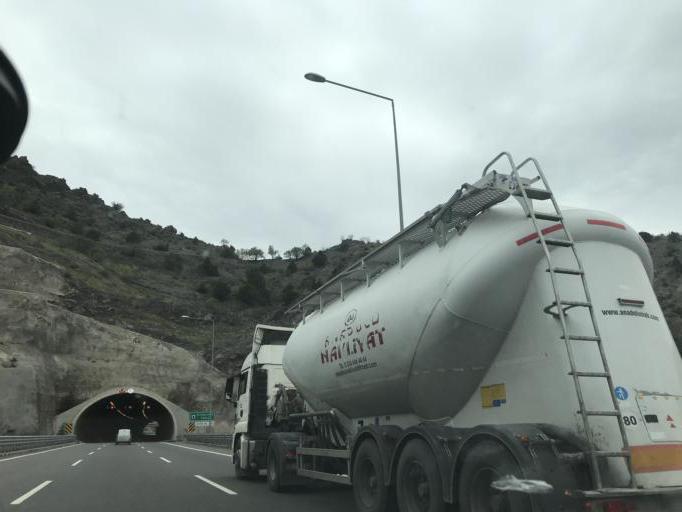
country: TR
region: Nigde
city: Ciftehan
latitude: 37.5573
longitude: 34.7656
